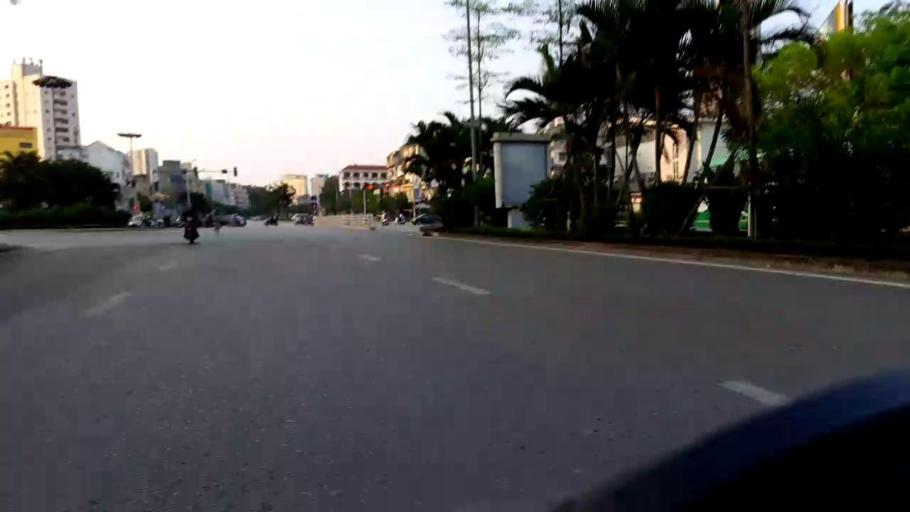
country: VN
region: Ha Noi
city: Cau Giay
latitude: 21.0398
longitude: 105.7977
